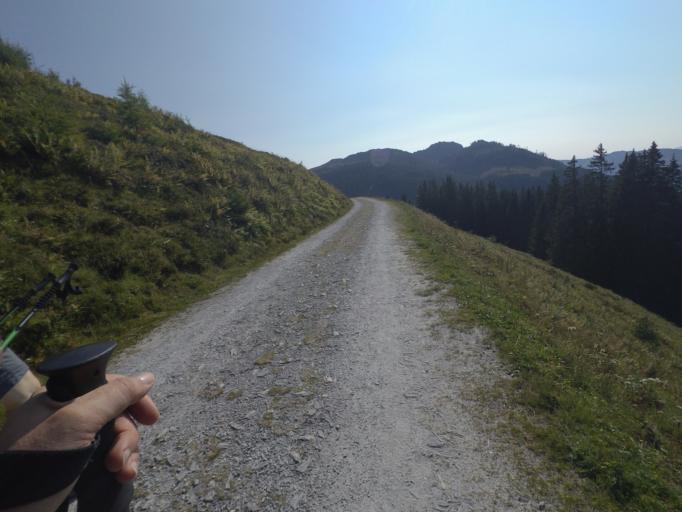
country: AT
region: Salzburg
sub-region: Politischer Bezirk Sankt Johann im Pongau
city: Kleinarl
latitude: 47.2768
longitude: 13.2570
